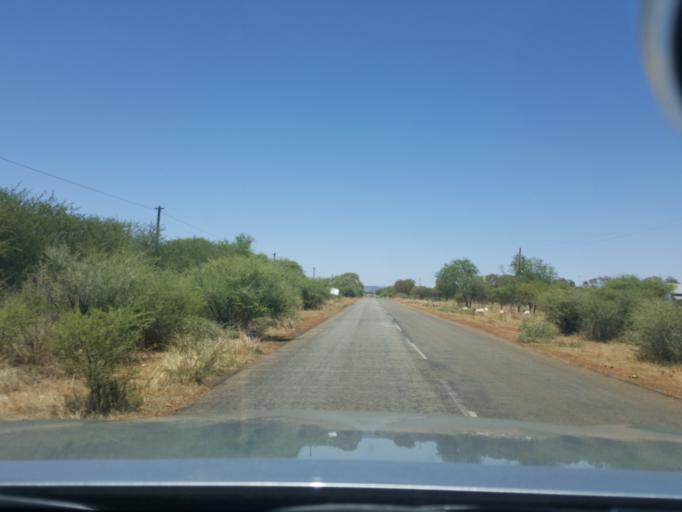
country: BW
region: South East
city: Otse
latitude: -25.1090
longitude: 25.9560
